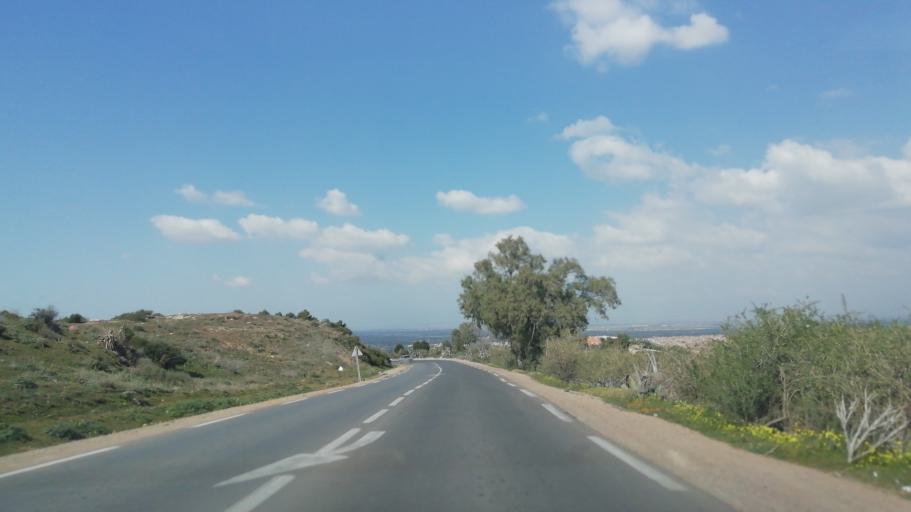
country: DZ
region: Mascara
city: Mascara
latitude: 35.5561
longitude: 0.0781
